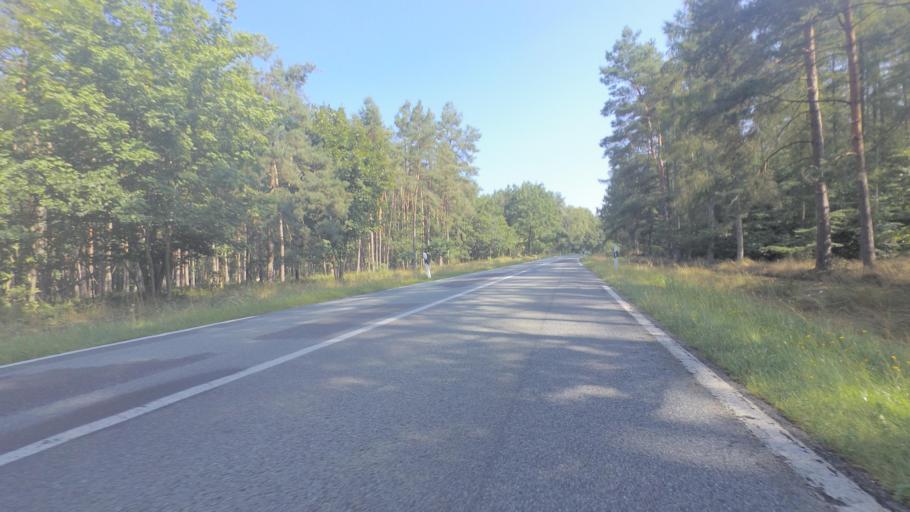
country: DE
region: Mecklenburg-Vorpommern
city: Malchow
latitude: 53.5811
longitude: 12.4633
